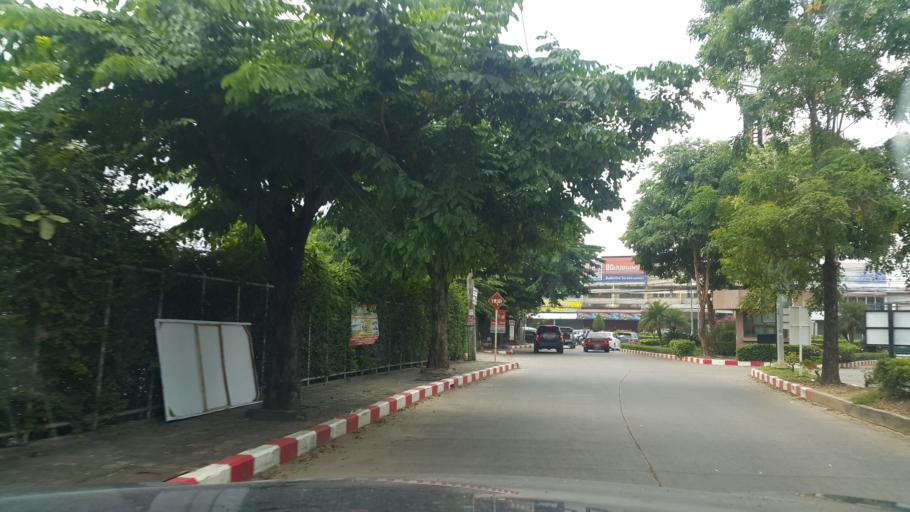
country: TH
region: Chiang Mai
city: Chiang Mai
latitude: 18.8080
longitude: 99.0234
